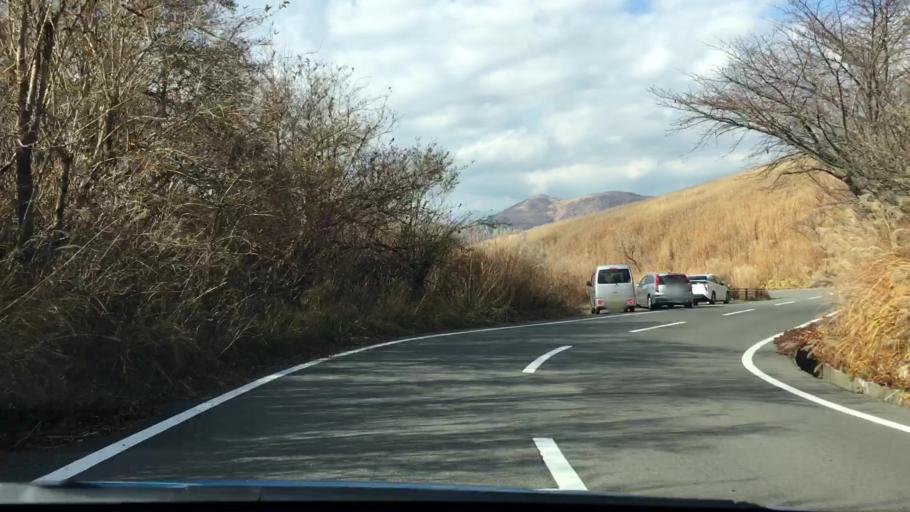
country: JP
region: Shizuoka
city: Gotemba
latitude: 35.4088
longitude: 138.9121
